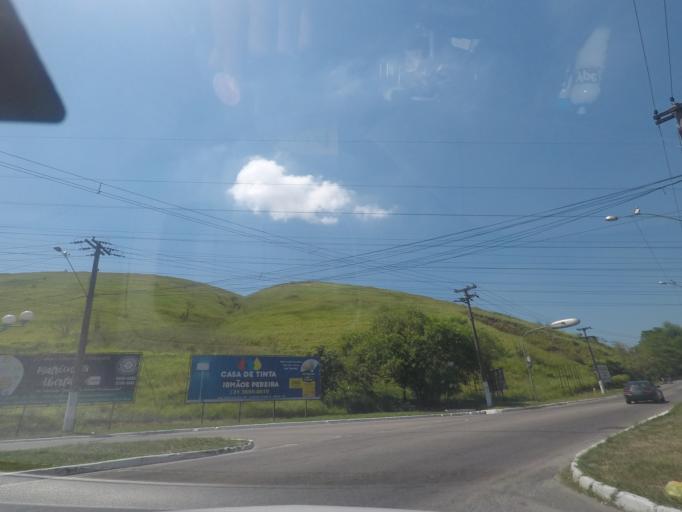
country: BR
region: Rio de Janeiro
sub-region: Petropolis
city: Petropolis
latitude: -22.6030
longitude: -43.1904
